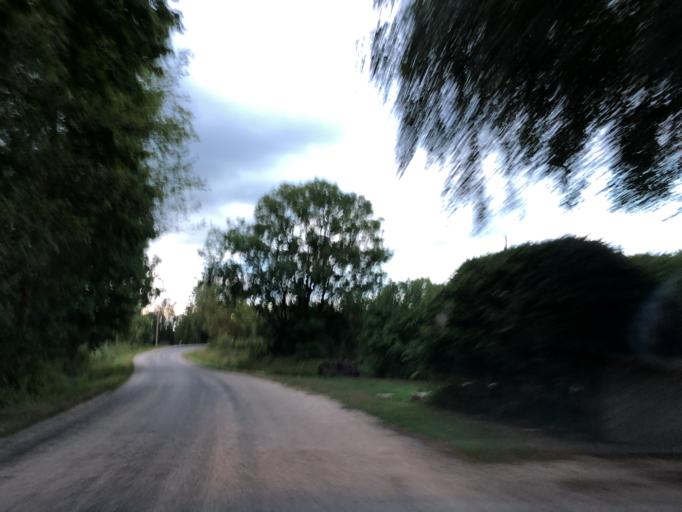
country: EE
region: Laeaene
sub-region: Ridala Parish
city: Uuemoisa
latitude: 58.8795
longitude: 23.6414
